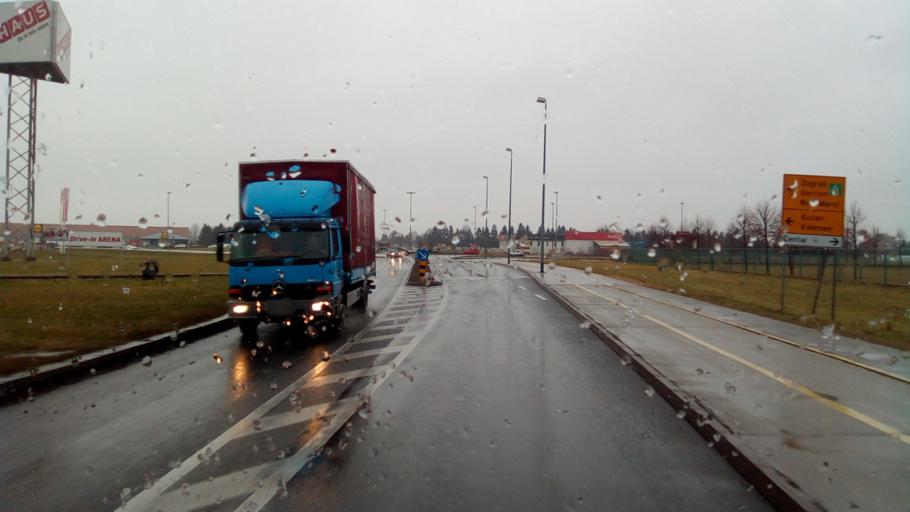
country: HR
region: Varazdinska
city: Varazdin
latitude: 46.2926
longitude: 16.3512
